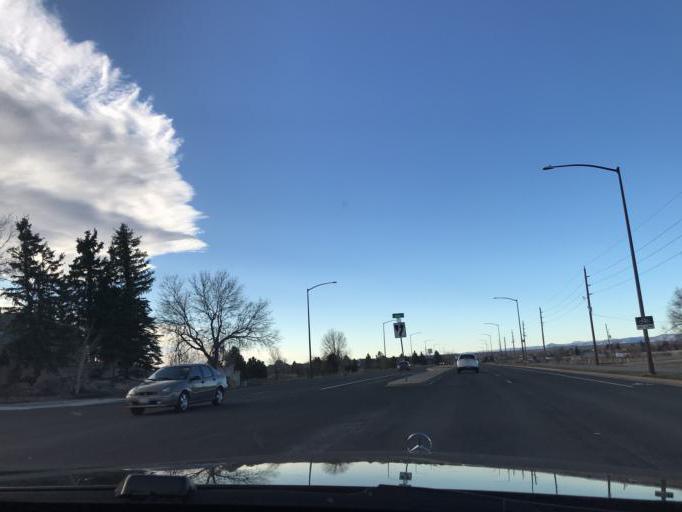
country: US
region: Colorado
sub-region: Boulder County
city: Superior
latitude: 39.9819
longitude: -105.1659
